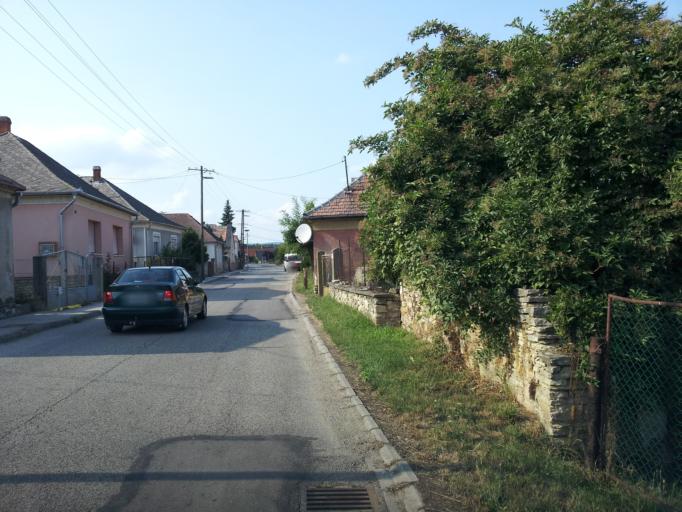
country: HU
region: Veszprem
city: Hajmasker
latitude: 47.1274
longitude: 18.0323
